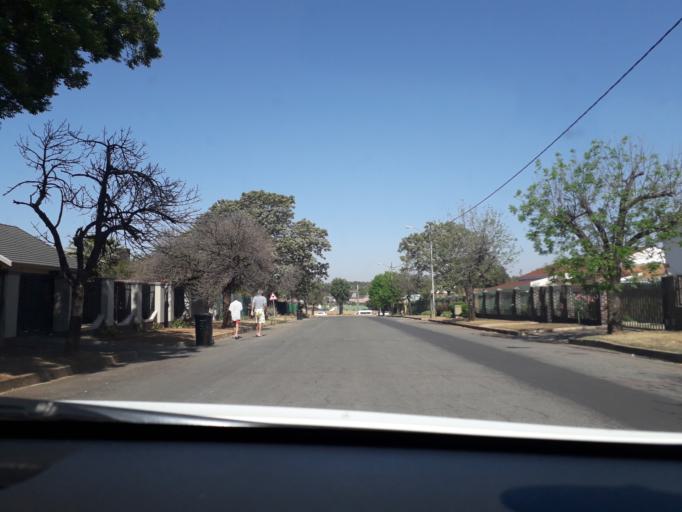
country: ZA
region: Gauteng
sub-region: City of Johannesburg Metropolitan Municipality
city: Modderfontein
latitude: -26.0922
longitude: 28.2228
